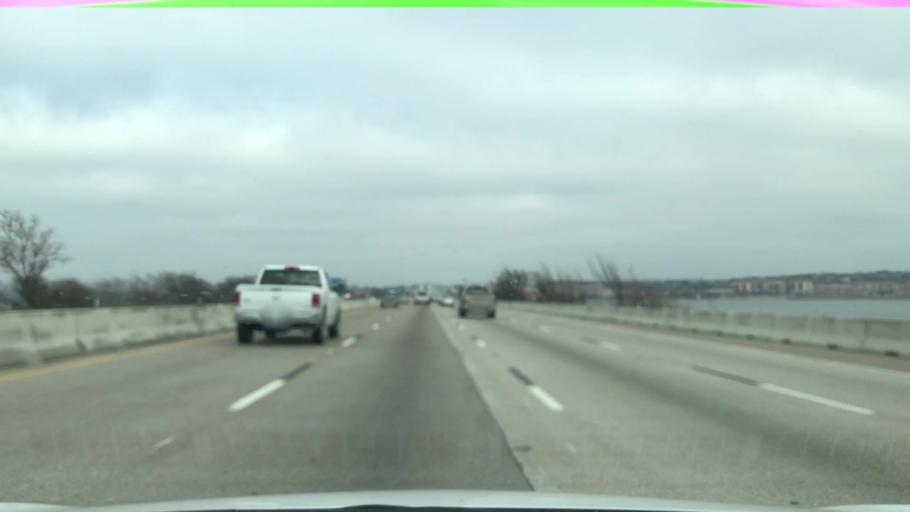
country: US
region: Texas
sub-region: Rockwall County
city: Heath
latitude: 32.8867
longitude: -96.4963
